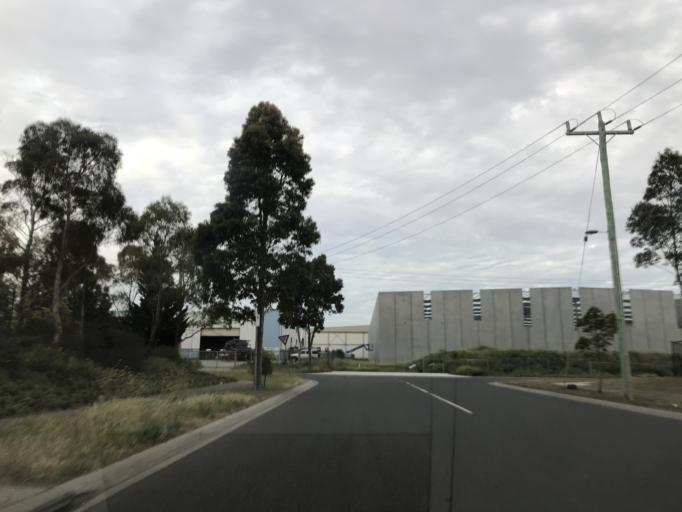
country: AU
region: Victoria
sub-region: Brimbank
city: Derrimut
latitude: -37.8100
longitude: 144.7828
